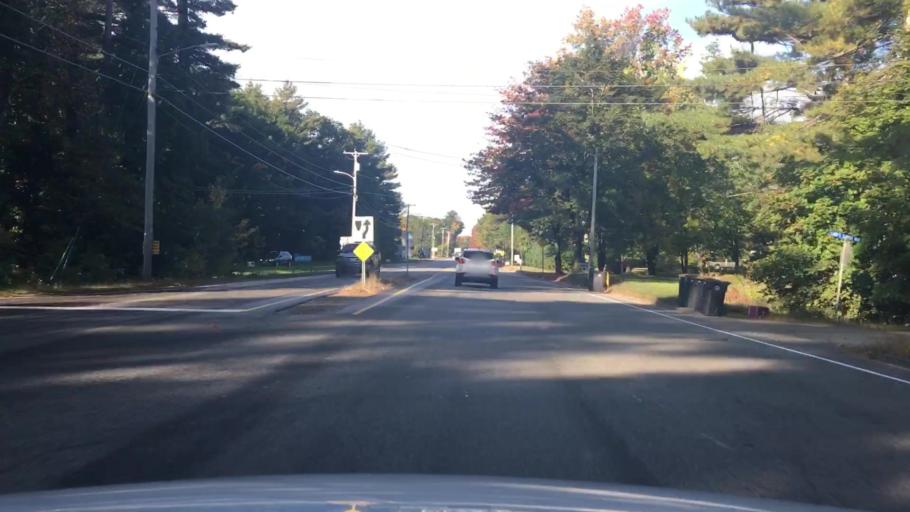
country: US
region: Maine
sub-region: Cumberland County
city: Westbrook
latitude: 43.6417
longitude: -70.4028
